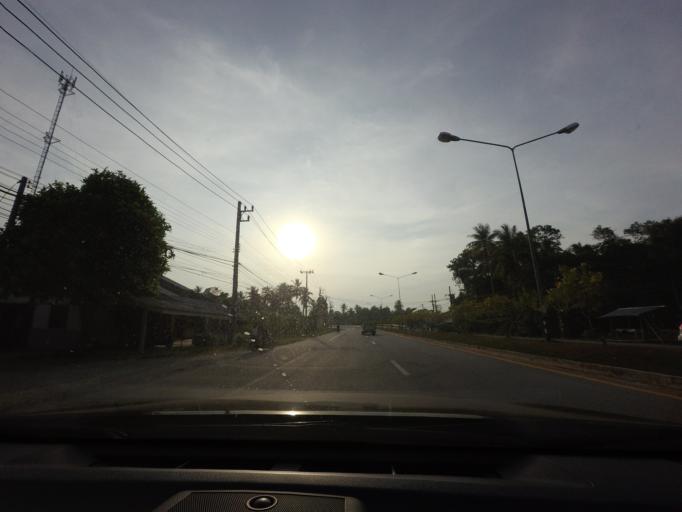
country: TH
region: Narathiwat
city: Narathiwat
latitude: 6.4168
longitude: 101.8479
